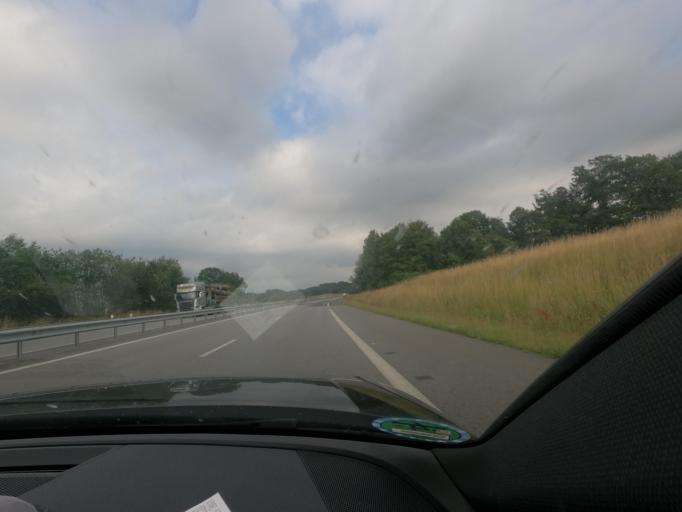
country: FR
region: Haute-Normandie
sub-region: Departement de la Seine-Maritime
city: Yerville
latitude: 49.6625
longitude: 0.9209
